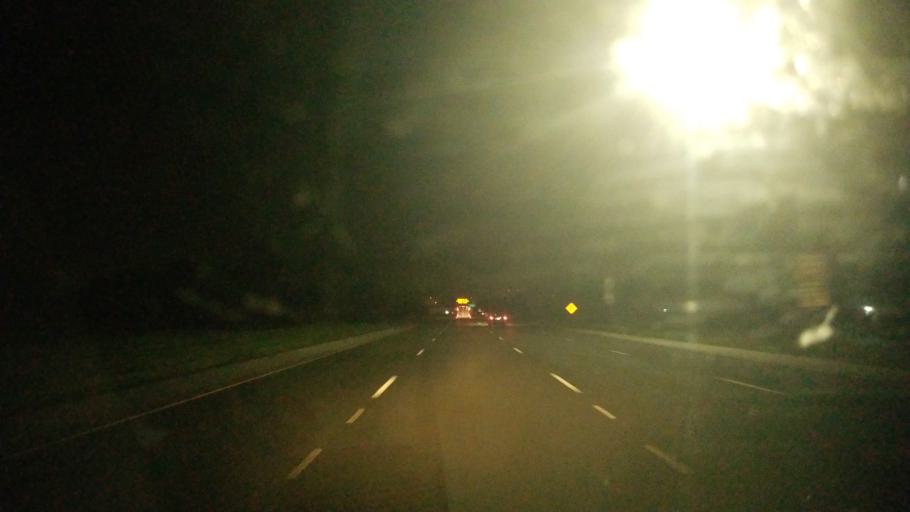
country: US
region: Illinois
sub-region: Madison County
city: Glen Carbon
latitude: 38.7568
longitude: -90.0184
